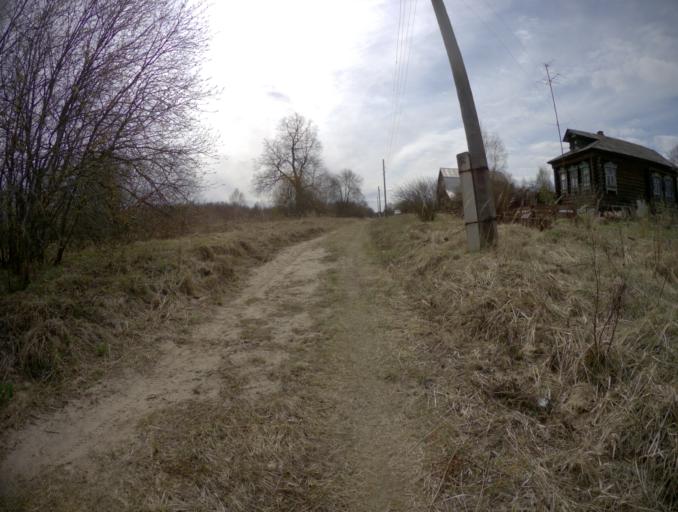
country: RU
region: Vladimir
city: Raduzhnyy
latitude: 55.8709
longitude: 40.2109
